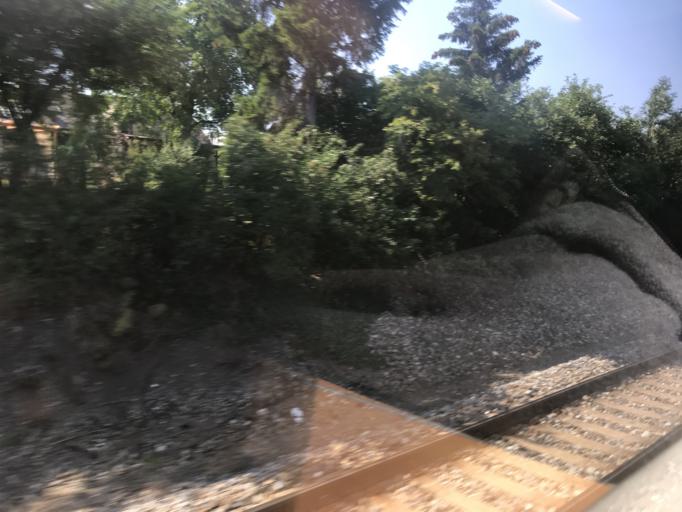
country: CZ
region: Praha
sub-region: Praha 8
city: Liben
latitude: 50.0669
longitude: 14.4826
